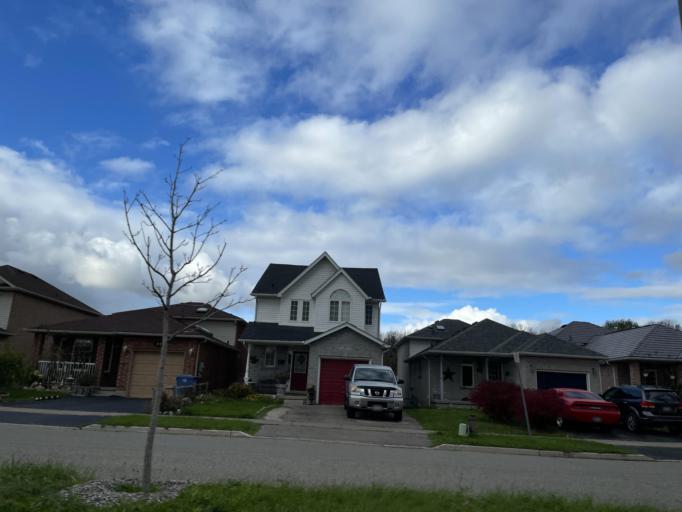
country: CA
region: Ontario
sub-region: Wellington County
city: Guelph
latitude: 43.5281
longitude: -80.2820
